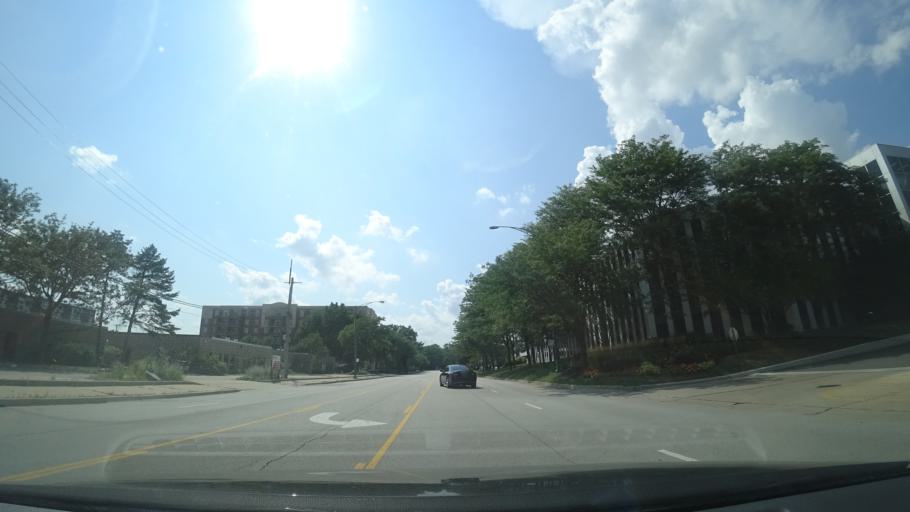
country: US
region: Illinois
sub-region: Cook County
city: Norridge
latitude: 41.9811
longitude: -87.8427
